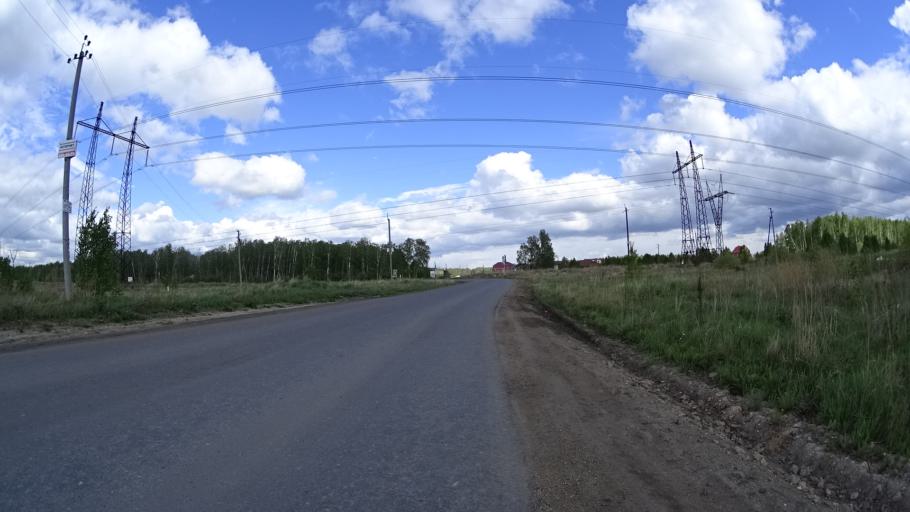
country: RU
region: Chelyabinsk
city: Sargazy
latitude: 55.1621
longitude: 61.2482
